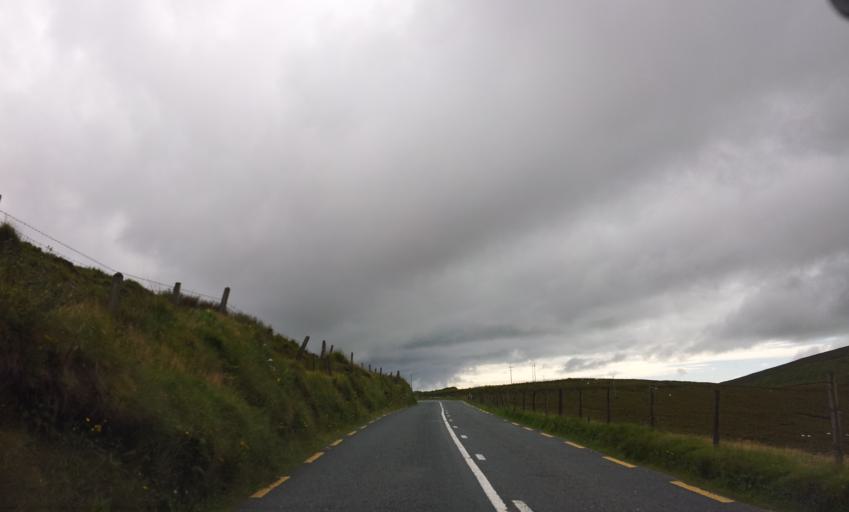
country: IE
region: Munster
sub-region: Ciarrai
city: Killorglin
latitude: 52.1993
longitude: -9.9295
